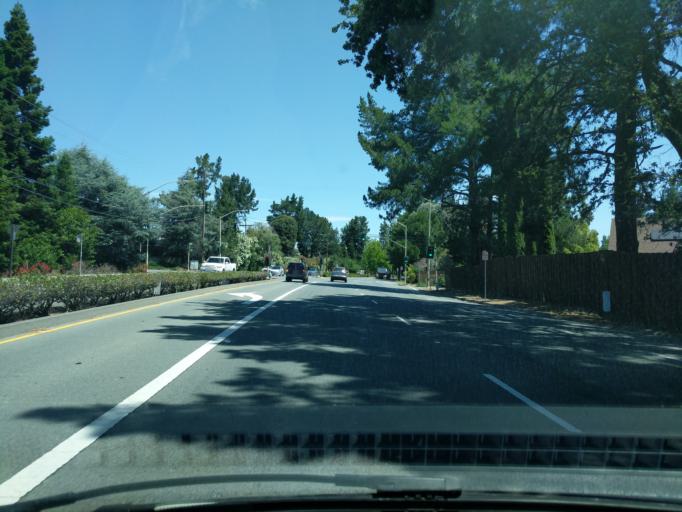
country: US
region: California
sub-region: Contra Costa County
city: Pleasant Hill
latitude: 37.9575
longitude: -122.0841
